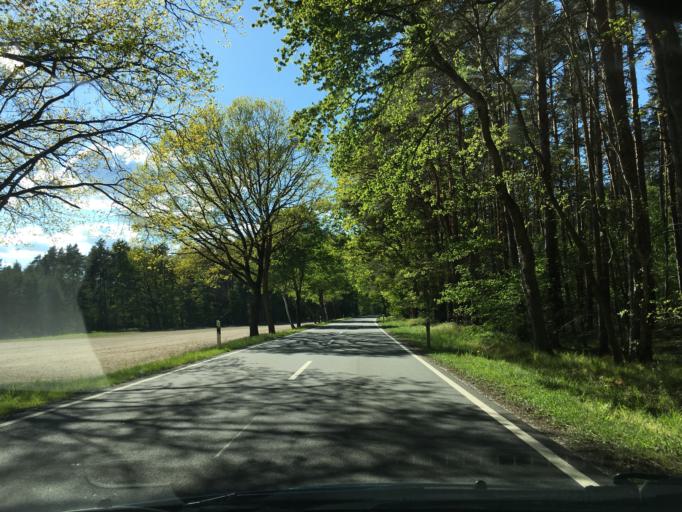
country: DE
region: Lower Saxony
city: Gartow
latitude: 53.0169
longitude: 11.5117
